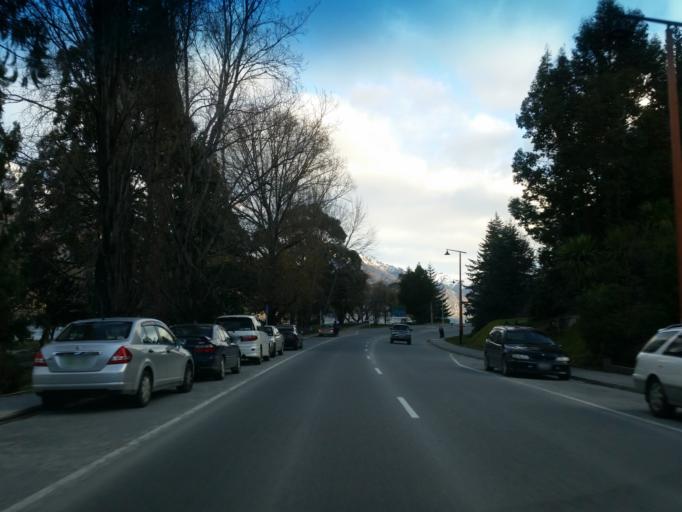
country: NZ
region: Otago
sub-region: Queenstown-Lakes District
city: Queenstown
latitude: -45.0365
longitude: 168.6498
